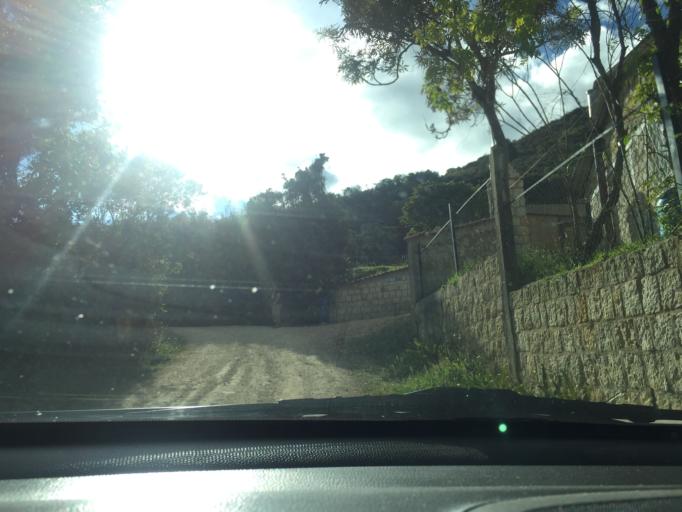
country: CO
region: Cundinamarca
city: Sopo
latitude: 4.9234
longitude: -73.9046
